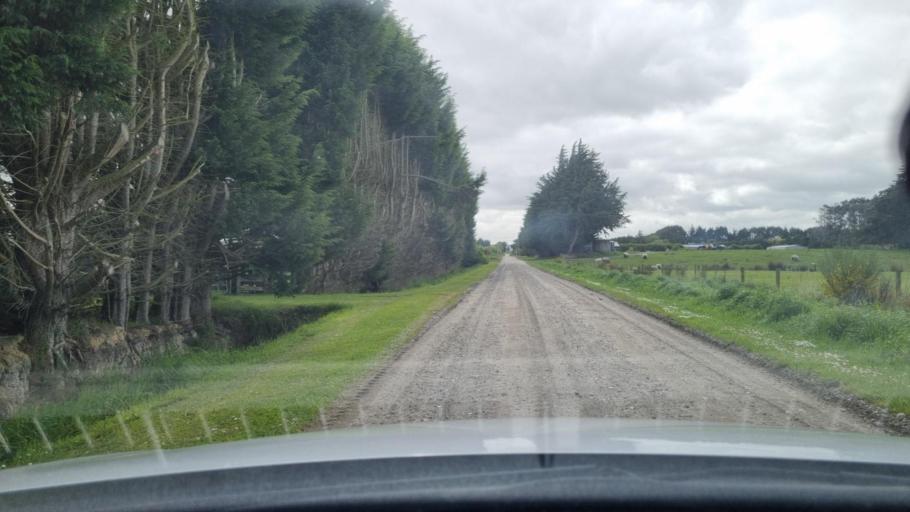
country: NZ
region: Southland
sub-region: Invercargill City
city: Invercargill
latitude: -46.4386
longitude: 168.3897
